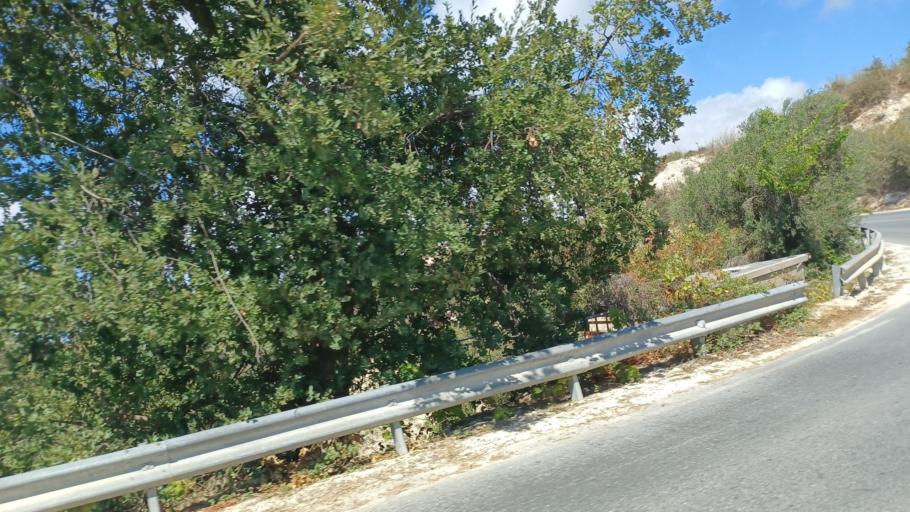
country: CY
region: Pafos
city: Tala
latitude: 34.8499
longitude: 32.4631
